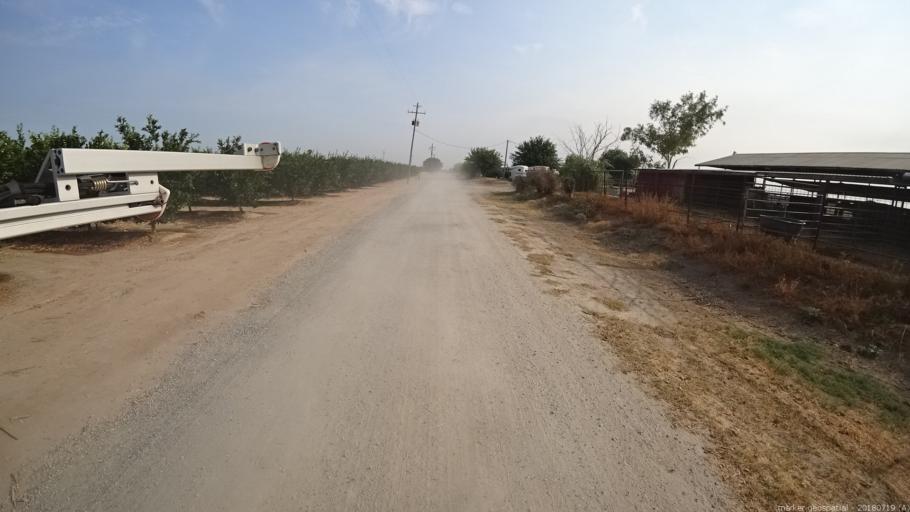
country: US
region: California
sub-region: Madera County
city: Fairmead
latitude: 37.1045
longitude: -120.1931
